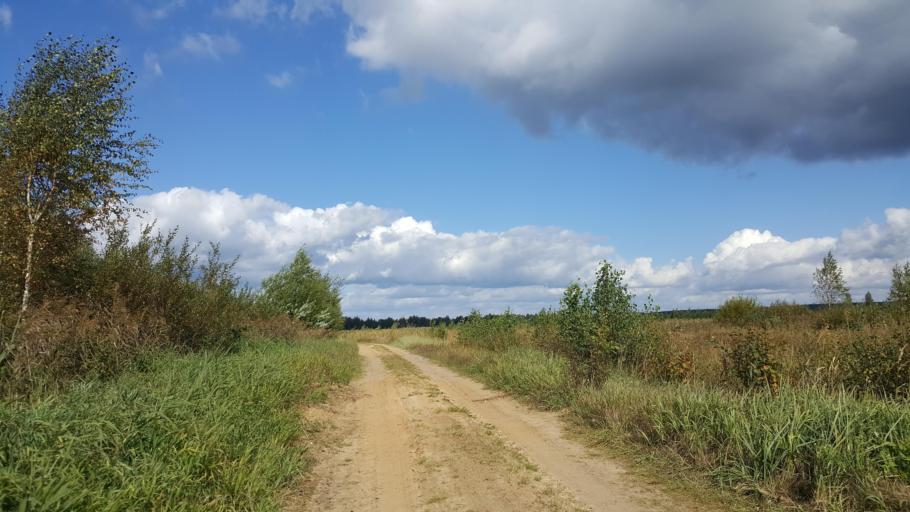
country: BY
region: Brest
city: Kamyanyets
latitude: 52.4547
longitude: 23.9347
